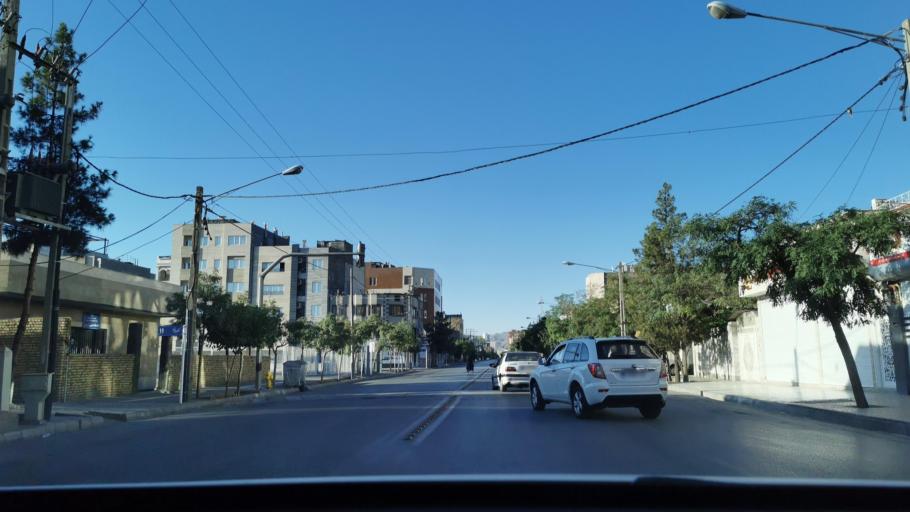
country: IR
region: Razavi Khorasan
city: Mashhad
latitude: 36.3549
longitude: 59.4973
